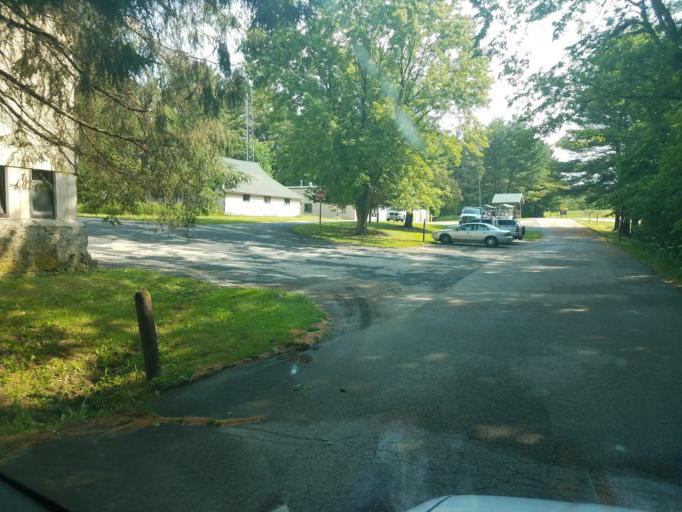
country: US
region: Wisconsin
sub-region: Monroe County
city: Cashton
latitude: 43.7012
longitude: -90.5711
